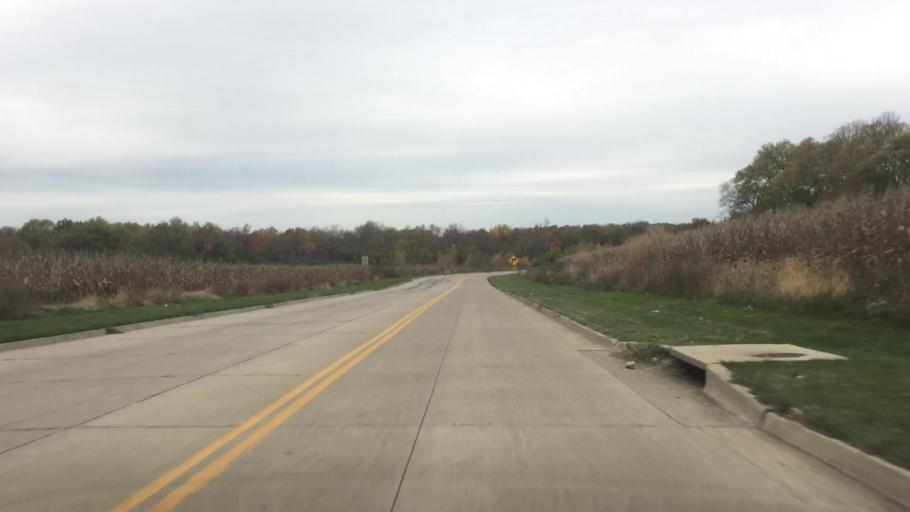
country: US
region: Missouri
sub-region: Jackson County
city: Greenwood
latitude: 38.8792
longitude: -94.3606
